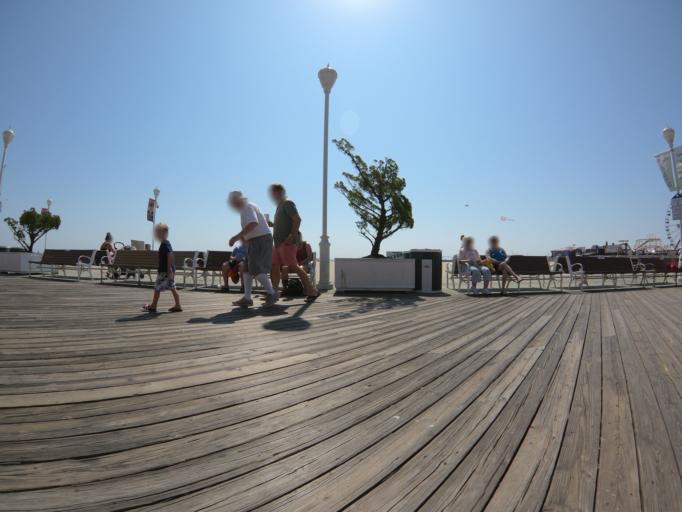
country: US
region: Maryland
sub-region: Worcester County
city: Ocean City
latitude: 38.3293
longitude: -75.0859
